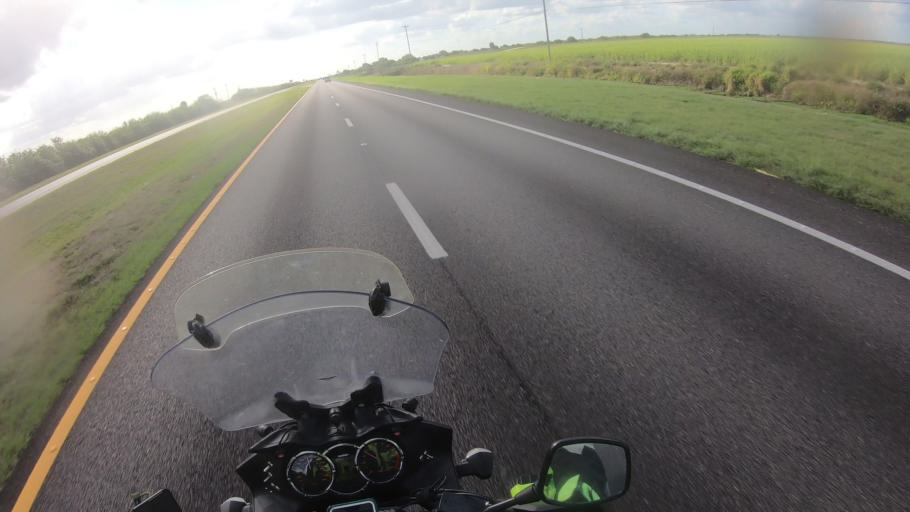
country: US
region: Florida
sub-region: Glades County
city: Moore Haven
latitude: 26.8330
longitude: -81.1346
